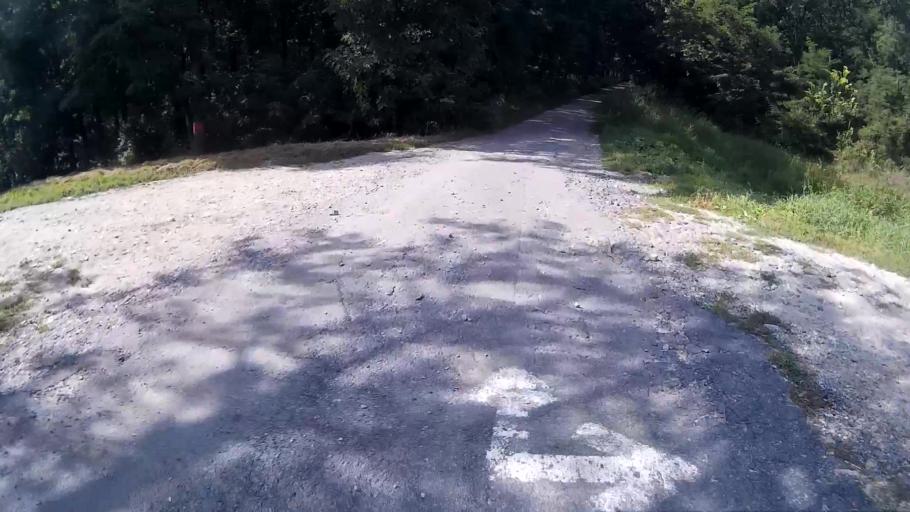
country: CZ
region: South Moravian
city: Hrusovany nad Jevisovkou
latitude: 48.7882
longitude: 16.4348
